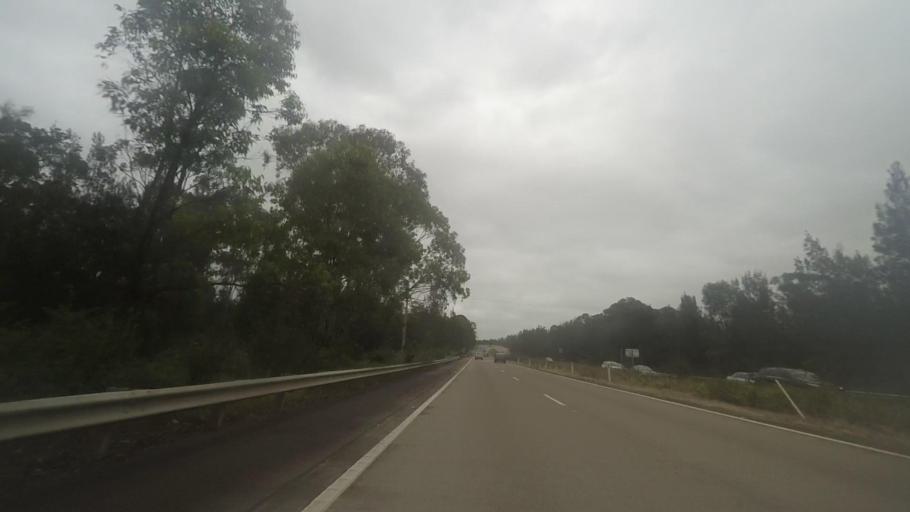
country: AU
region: New South Wales
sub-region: Port Stephens Shire
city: Medowie
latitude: -32.6800
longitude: 151.8187
